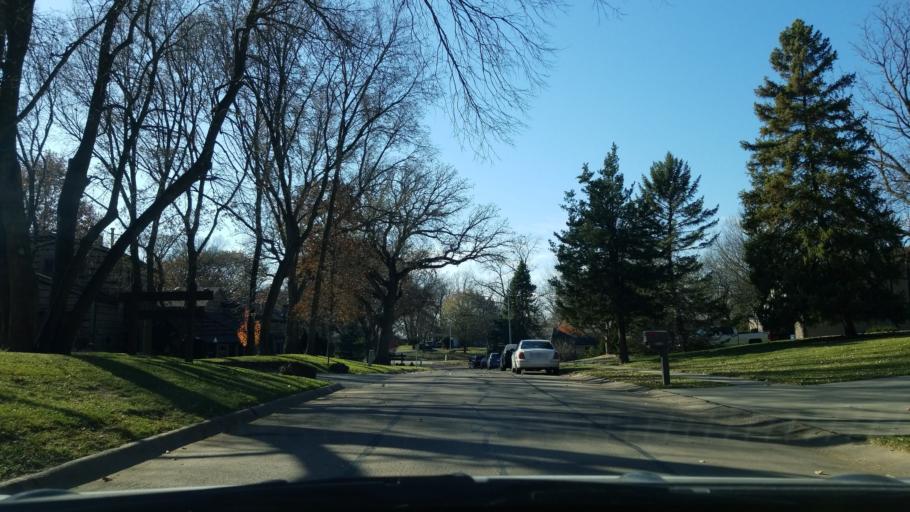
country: US
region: Nebraska
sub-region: Sarpy County
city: Bellevue
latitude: 41.1639
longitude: -95.8988
